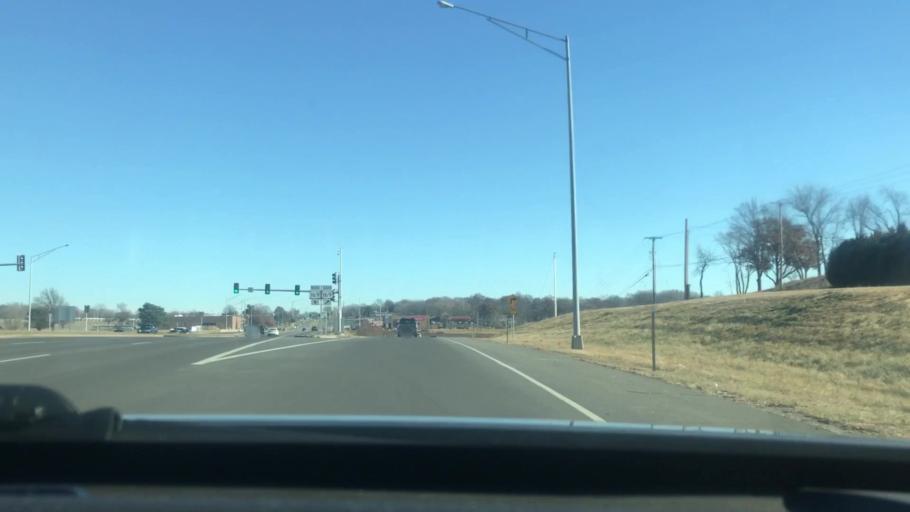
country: US
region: Missouri
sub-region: Clay County
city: Gladstone
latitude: 39.2463
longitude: -94.5937
